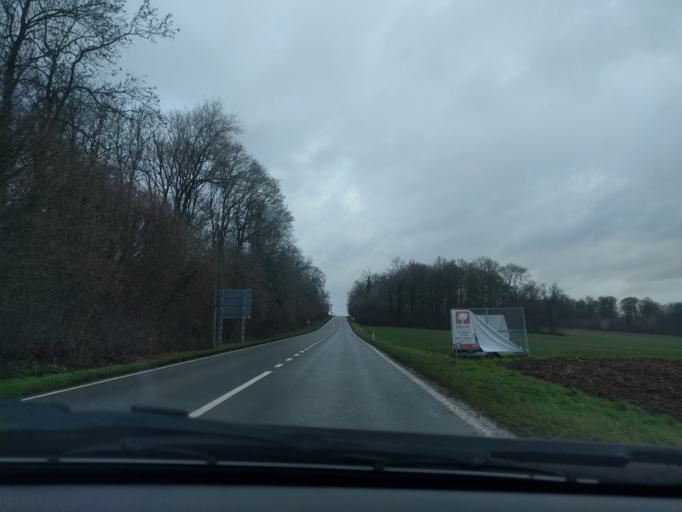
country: BE
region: Wallonia
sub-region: Province de Namur
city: Noville-les-Bois
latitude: 50.5094
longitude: 4.9709
